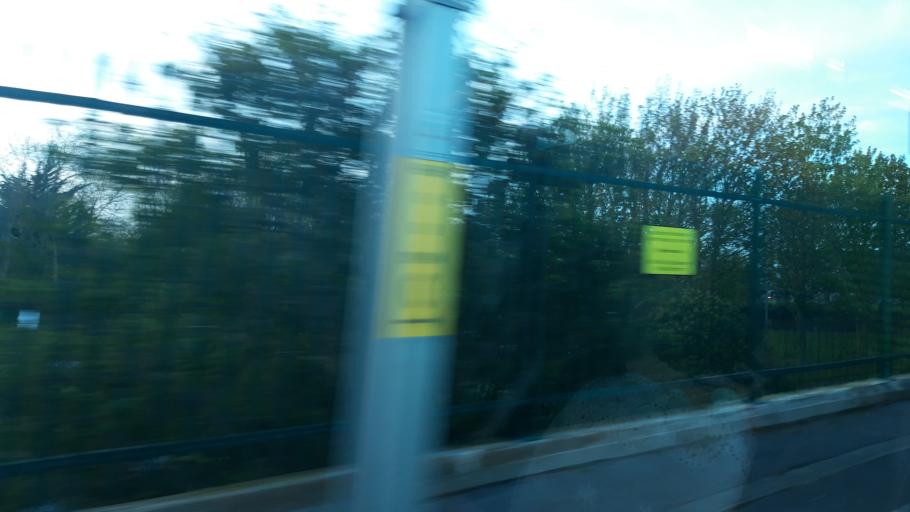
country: IE
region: Leinster
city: Donaghmede
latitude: 53.3919
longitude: -6.1541
